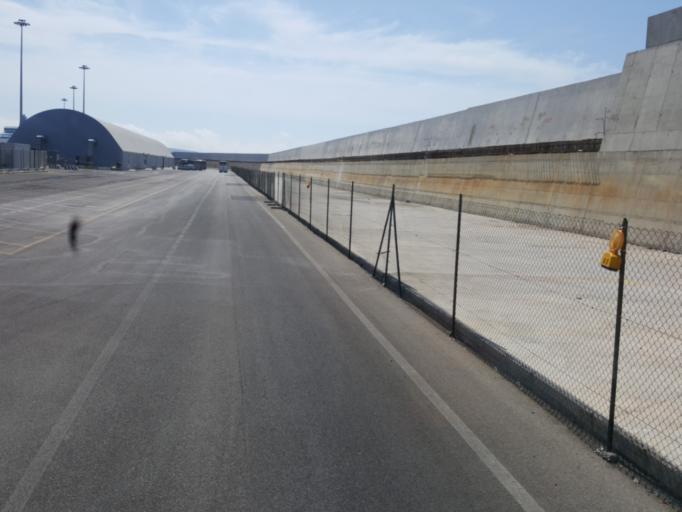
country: IT
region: Latium
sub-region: Citta metropolitana di Roma Capitale
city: Civitavecchia
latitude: 42.0954
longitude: 11.7766
